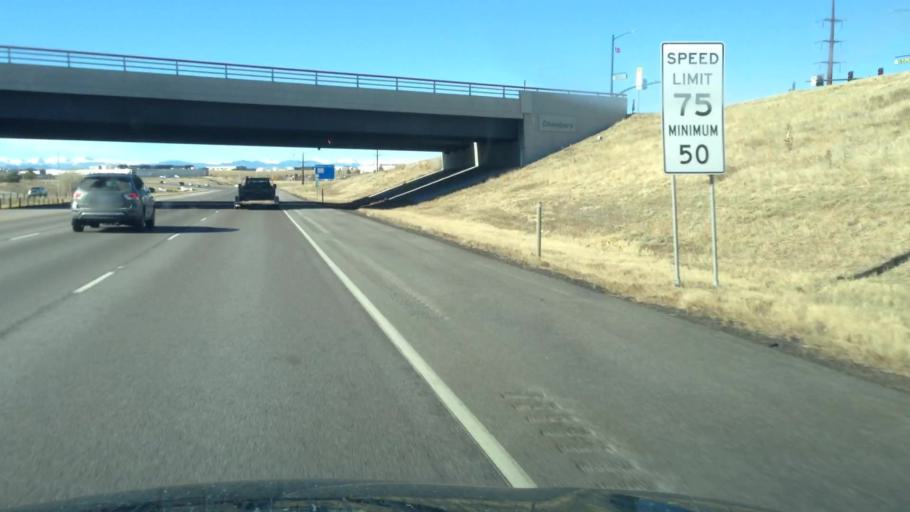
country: US
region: Colorado
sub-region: Douglas County
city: Stonegate
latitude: 39.5528
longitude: -104.8072
